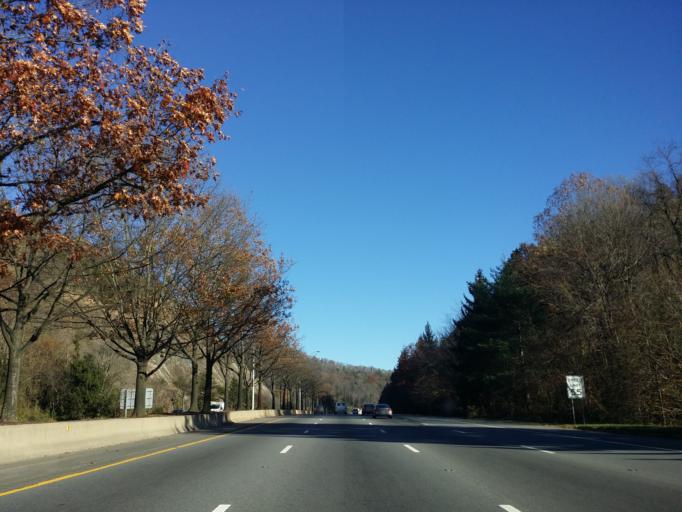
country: US
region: North Carolina
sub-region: Buncombe County
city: Asheville
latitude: 35.6000
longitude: -82.5412
